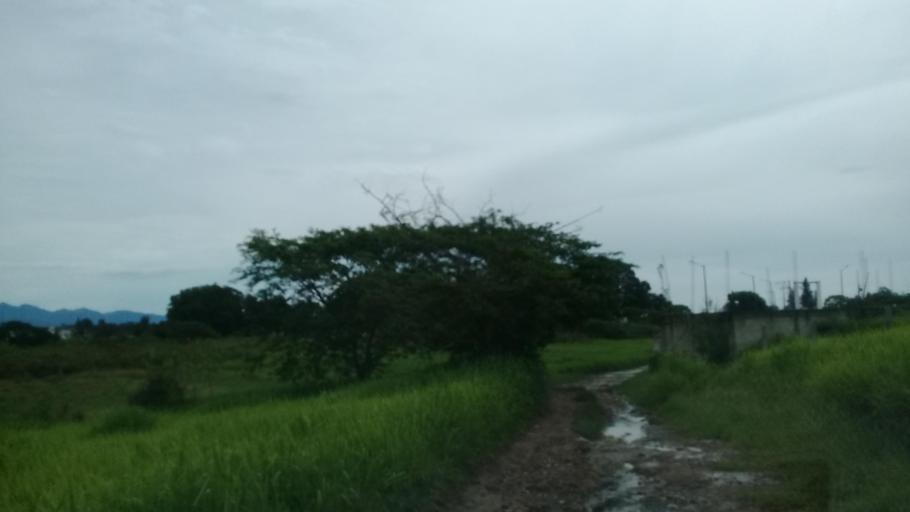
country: MX
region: Veracruz
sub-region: Emiliano Zapata
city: Dos Rios
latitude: 19.4803
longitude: -96.8021
